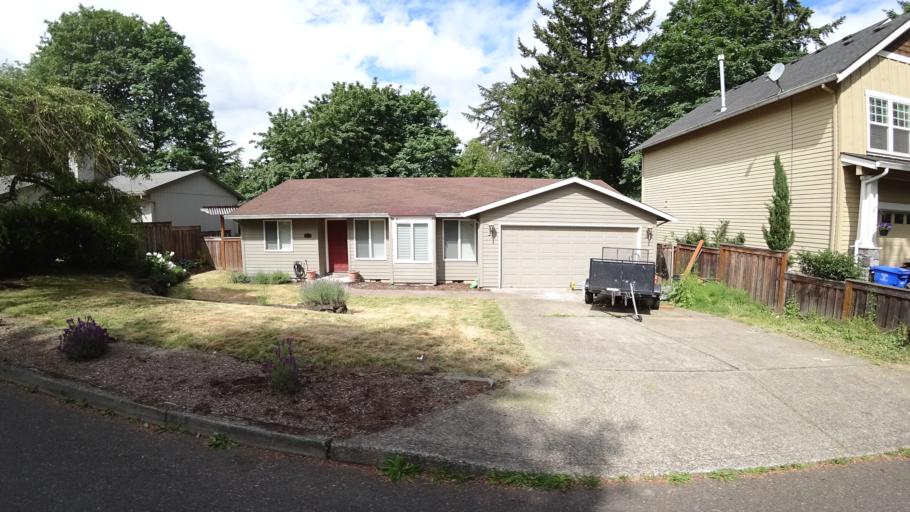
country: US
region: Oregon
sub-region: Clackamas County
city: Lake Oswego
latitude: 45.4552
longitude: -122.6866
